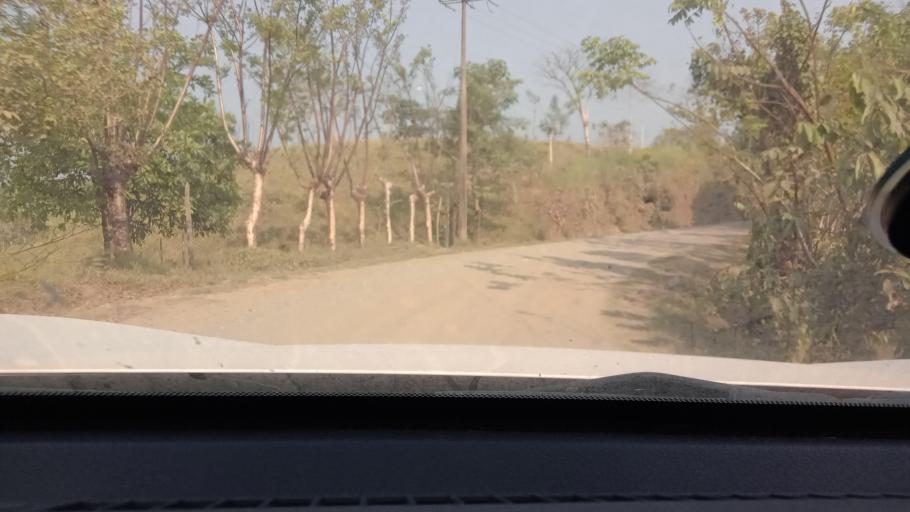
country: MX
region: Tabasco
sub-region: Huimanguillo
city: Francisco Rueda
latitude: 17.6547
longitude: -93.8905
